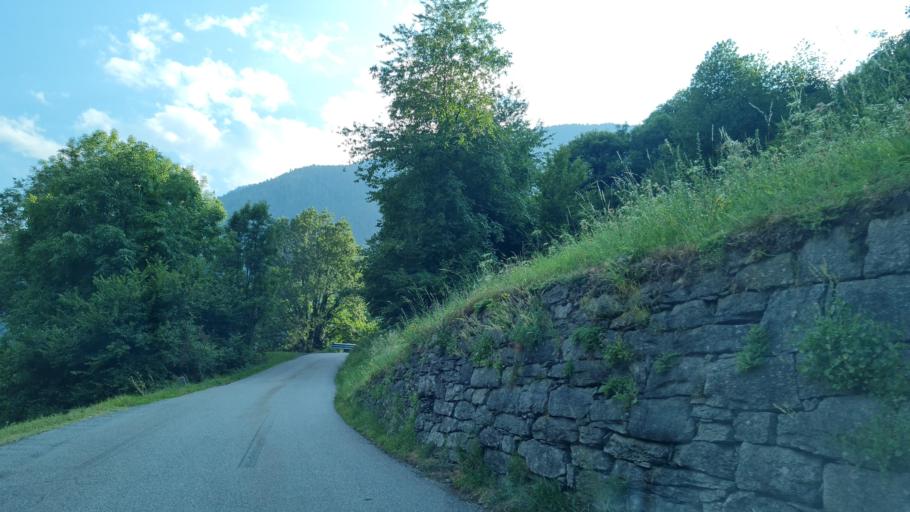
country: IT
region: Piedmont
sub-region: Provincia Verbano-Cusio-Ossola
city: Crodo
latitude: 46.2235
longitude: 8.3149
